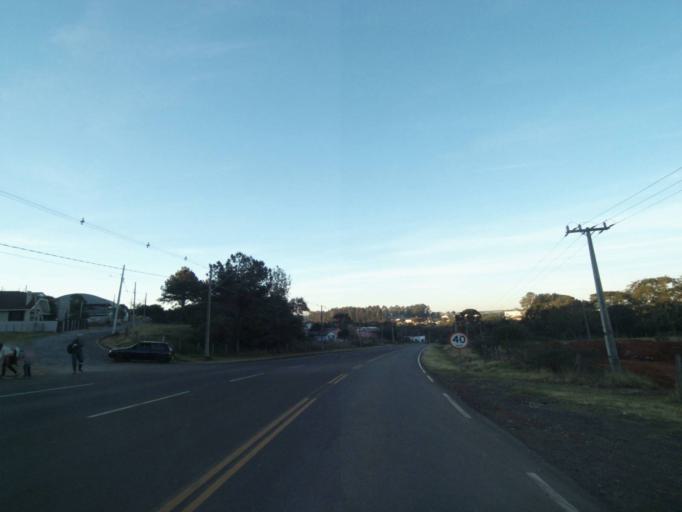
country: BR
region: Parana
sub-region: Tibagi
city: Tibagi
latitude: -24.5136
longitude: -50.4240
